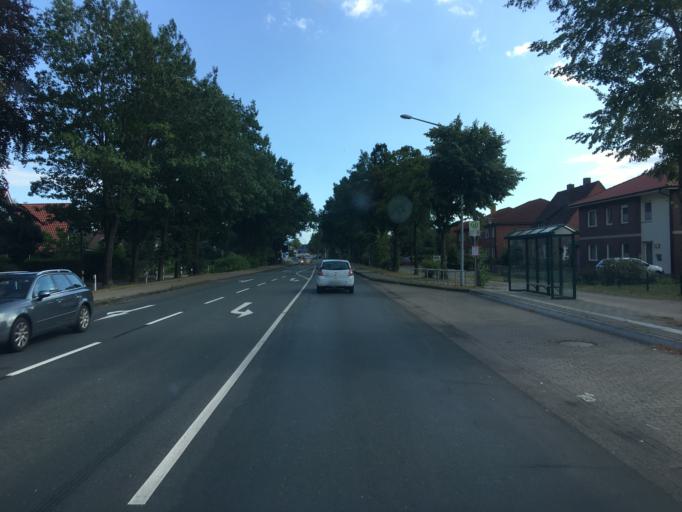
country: DE
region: Lower Saxony
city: Wardenburg
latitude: 53.0595
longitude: 8.1981
